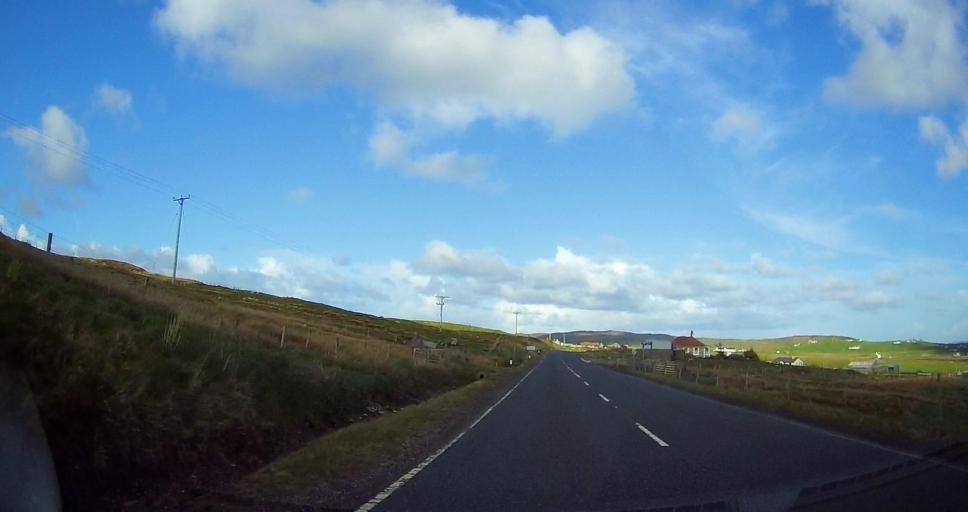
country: GB
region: Scotland
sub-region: Shetland Islands
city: Lerwick
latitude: 60.3534
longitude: -1.1748
